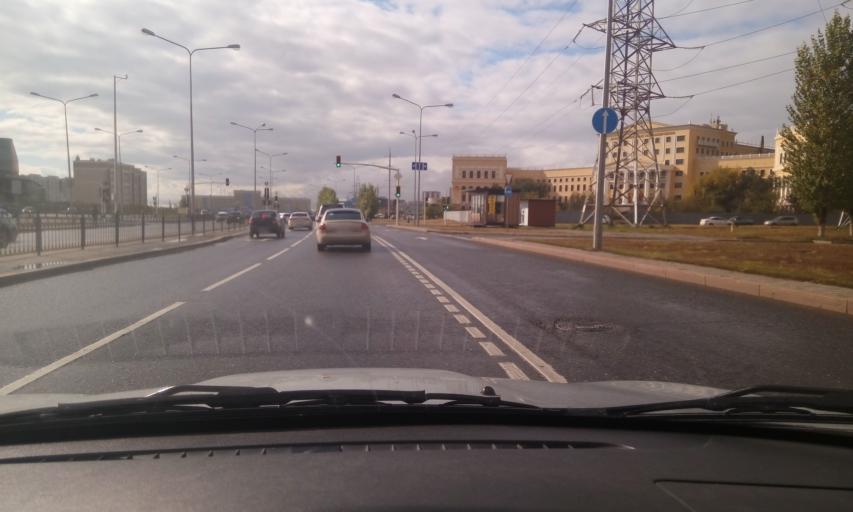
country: KZ
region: Astana Qalasy
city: Astana
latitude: 51.1484
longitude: 71.3839
